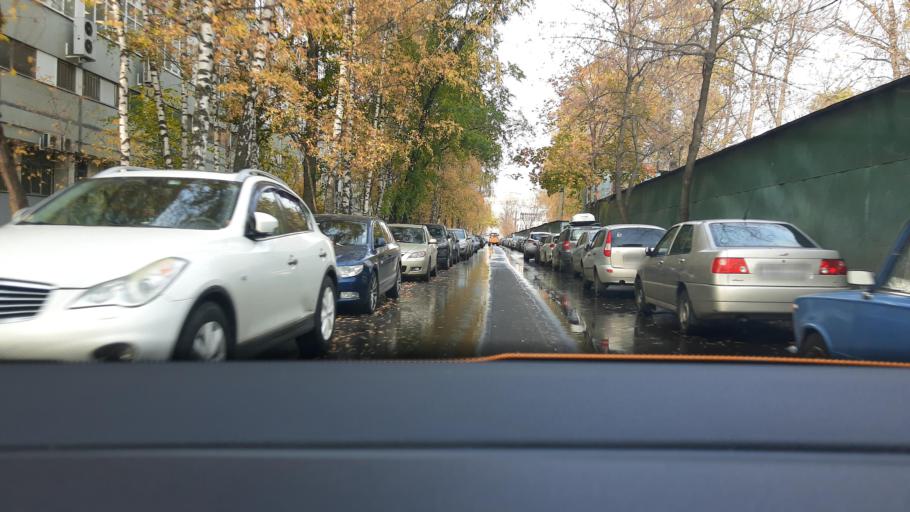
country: RU
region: Moscow
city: Sviblovo
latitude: 55.8585
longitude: 37.6254
